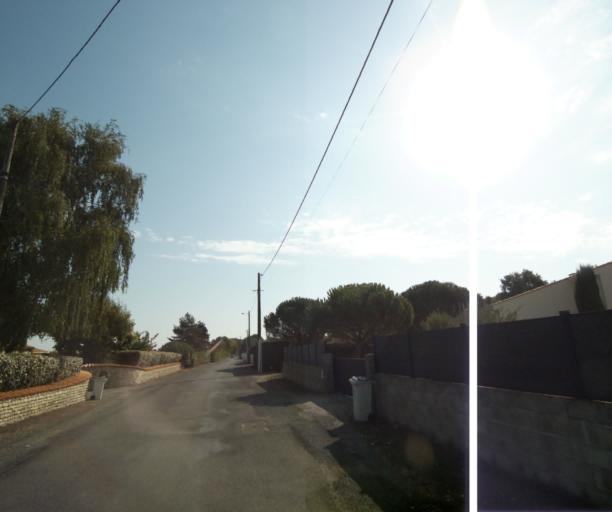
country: FR
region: Poitou-Charentes
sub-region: Departement de la Charente-Maritime
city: Tonnay-Charente
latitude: 45.9660
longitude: -0.8701
